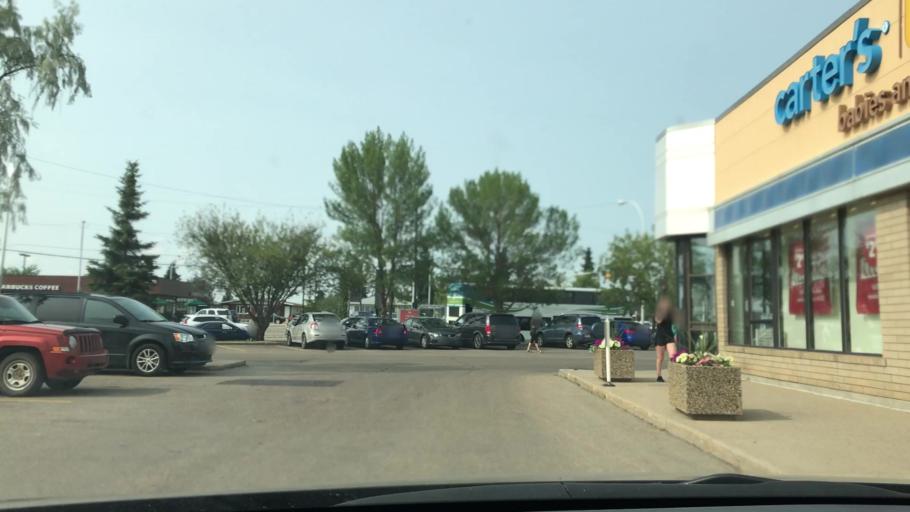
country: CA
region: Alberta
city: Edmonton
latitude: 53.5400
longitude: -113.4236
